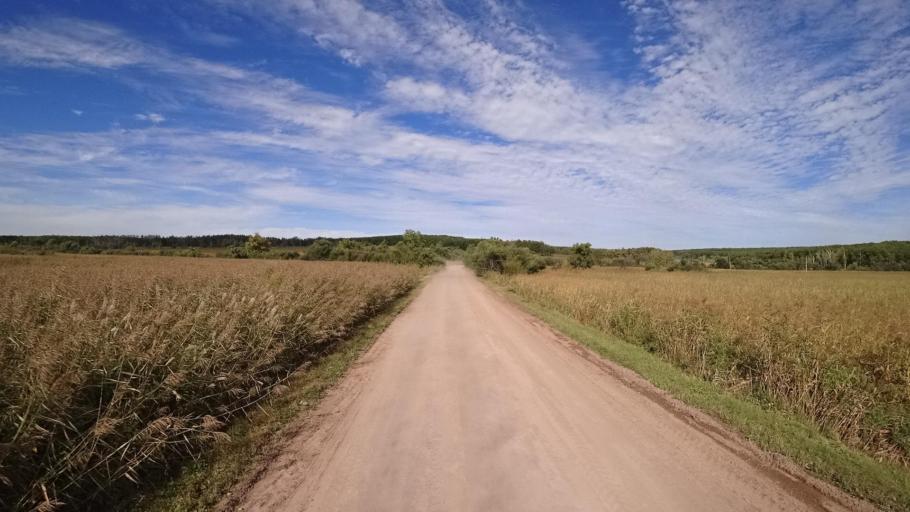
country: RU
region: Primorskiy
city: Yakovlevka
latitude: 44.3872
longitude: 133.5397
